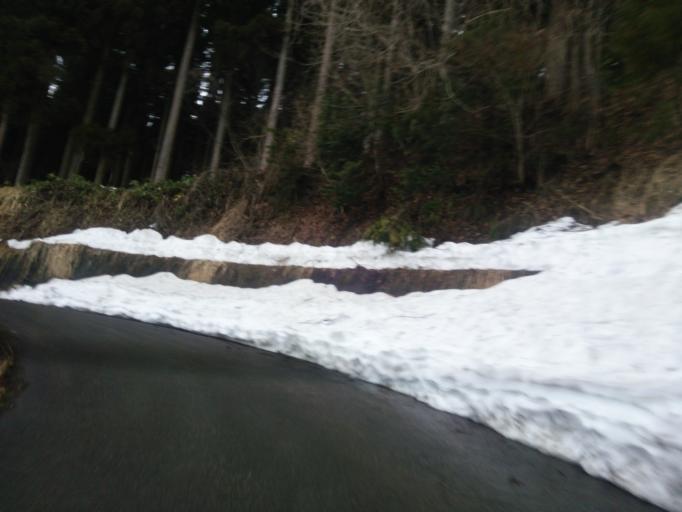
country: JP
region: Fukushima
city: Kitakata
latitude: 37.6971
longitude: 139.9444
